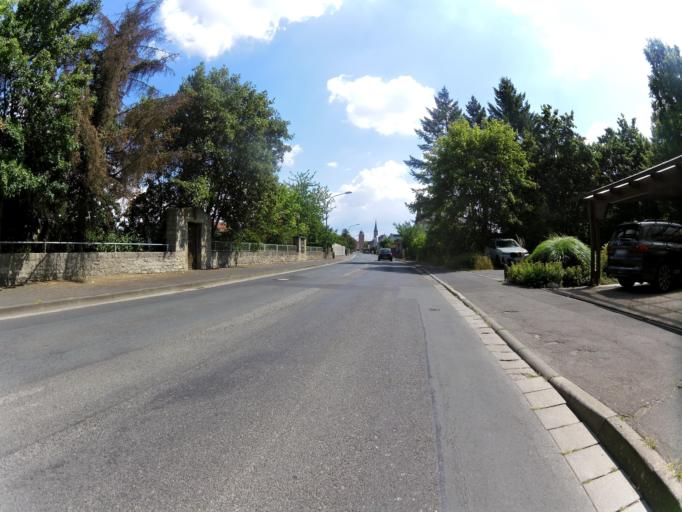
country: DE
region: Bavaria
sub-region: Regierungsbezirk Unterfranken
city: Ochsenfurt
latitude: 49.6657
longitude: 10.0556
